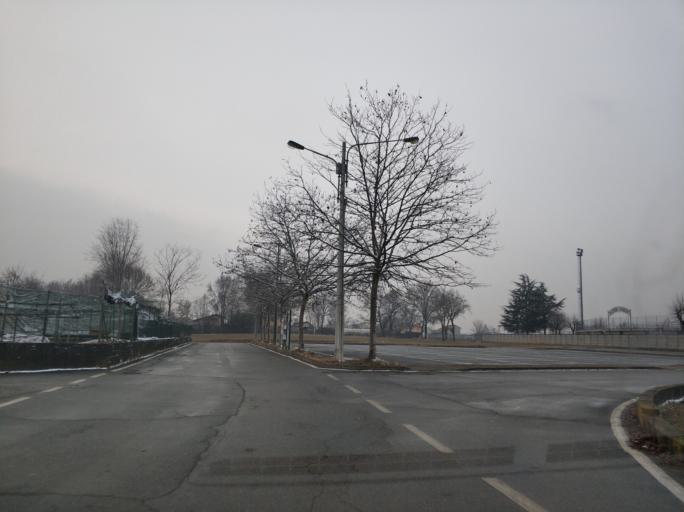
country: IT
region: Piedmont
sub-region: Provincia di Torino
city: San Francesco al Campo
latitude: 45.2321
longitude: 7.6598
